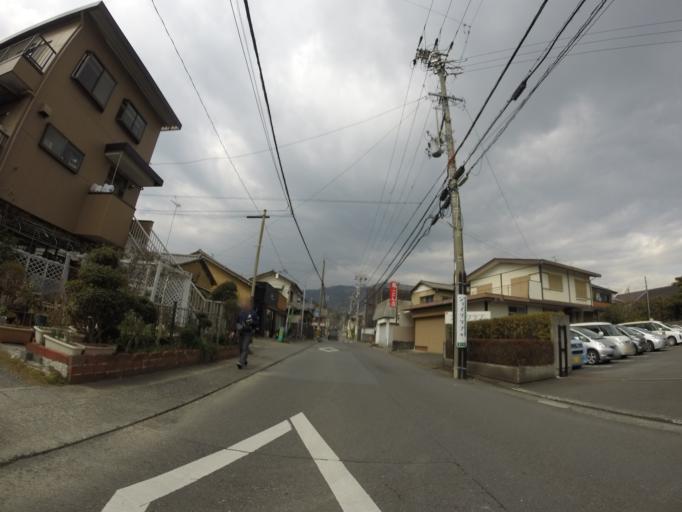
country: JP
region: Shizuoka
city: Shizuoka-shi
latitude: 35.0355
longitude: 138.4501
